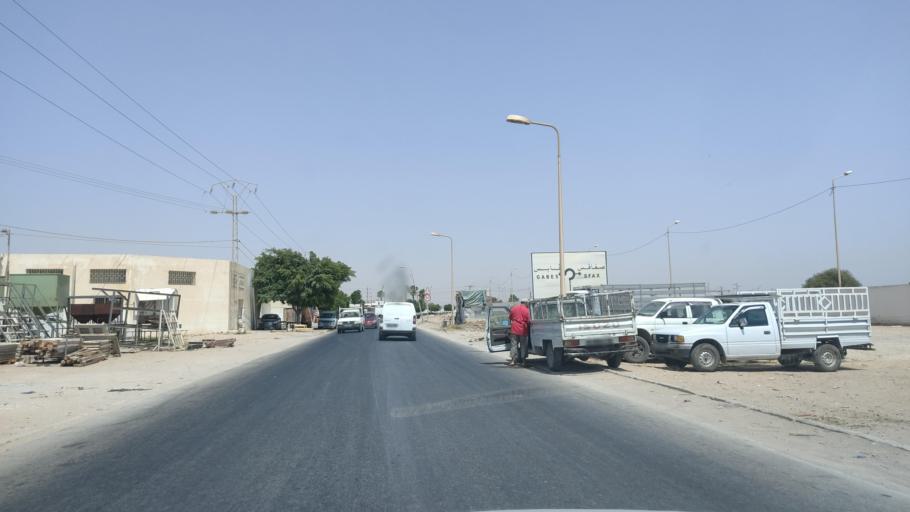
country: TN
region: Safaqis
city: Sfax
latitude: 34.6979
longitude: 10.7203
